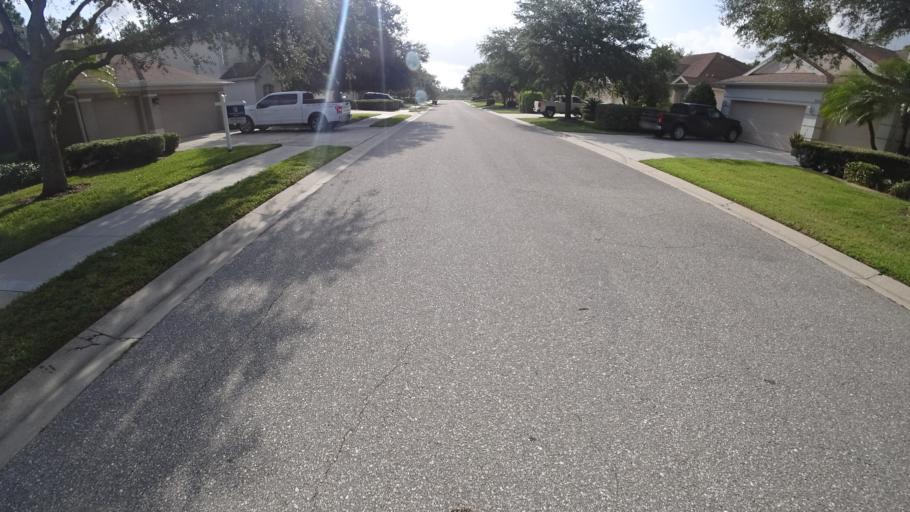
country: US
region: Florida
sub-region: Sarasota County
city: North Sarasota
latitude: 27.4213
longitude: -82.5068
